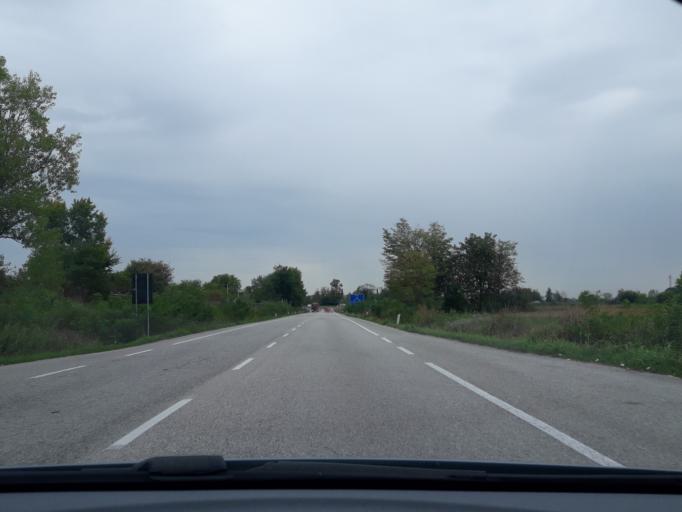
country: IT
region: Friuli Venezia Giulia
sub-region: Provincia di Udine
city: Povoletto
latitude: 46.1142
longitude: 13.2681
